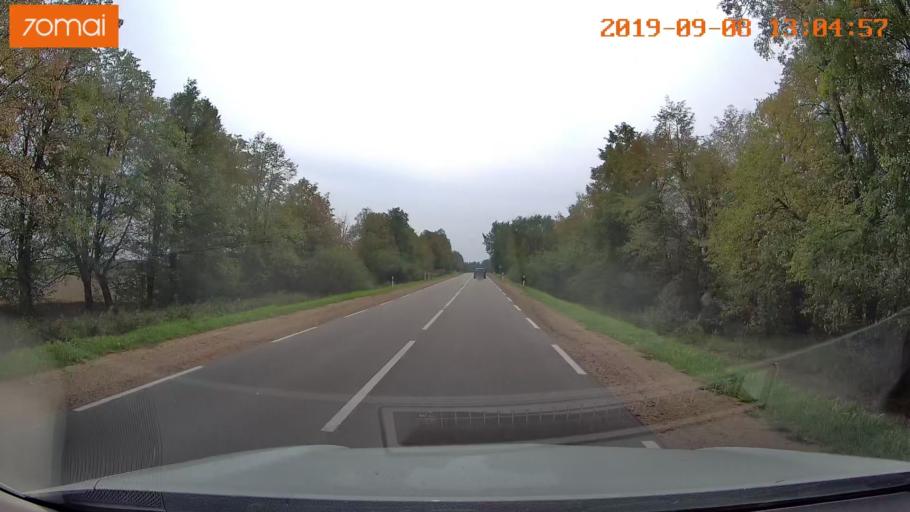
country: LT
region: Kauno apskritis
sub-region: Kauno rajonas
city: Karmelava
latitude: 54.8605
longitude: 24.2357
